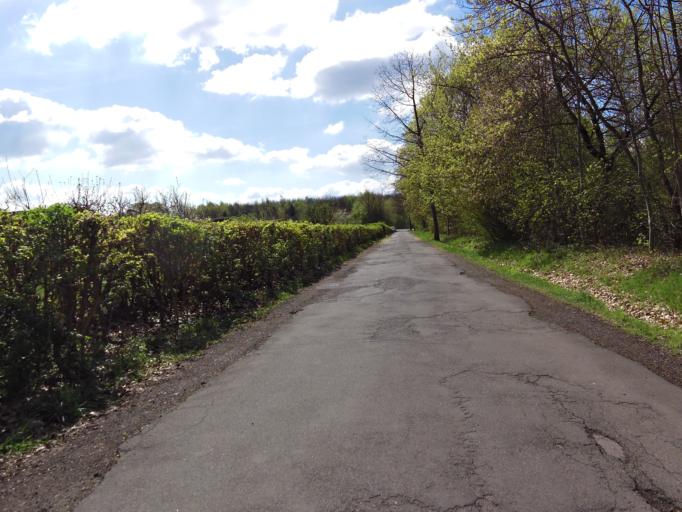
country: DE
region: Saxony
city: Leipzig
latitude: 51.3327
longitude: 12.4301
